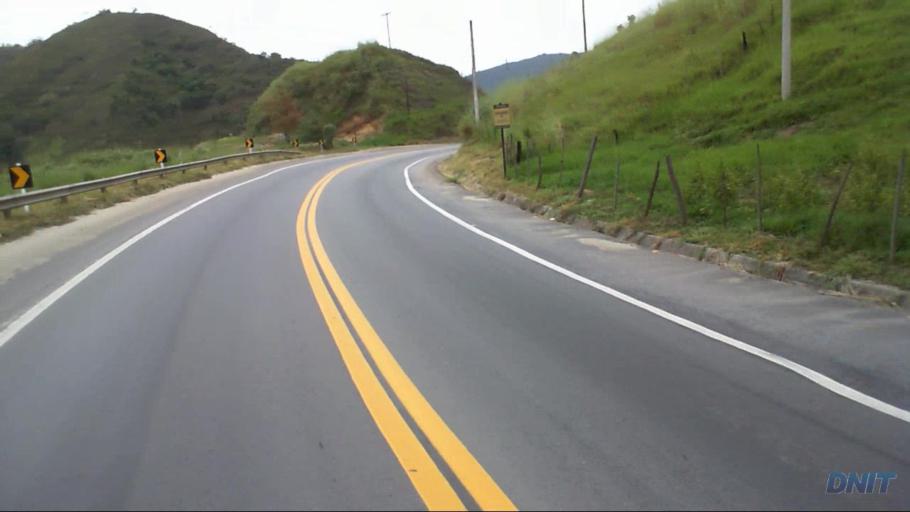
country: BR
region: Minas Gerais
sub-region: Timoteo
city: Timoteo
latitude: -19.6156
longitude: -42.7924
